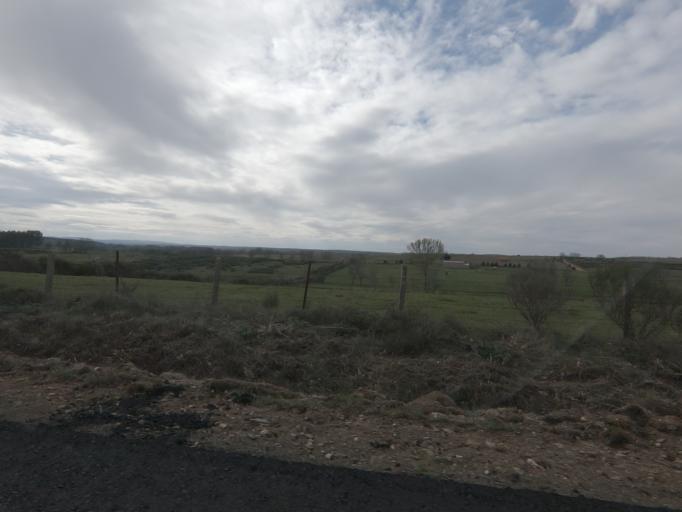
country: ES
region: Castille and Leon
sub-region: Provincia de Salamanca
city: Villasrubias
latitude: 40.3520
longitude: -6.6313
